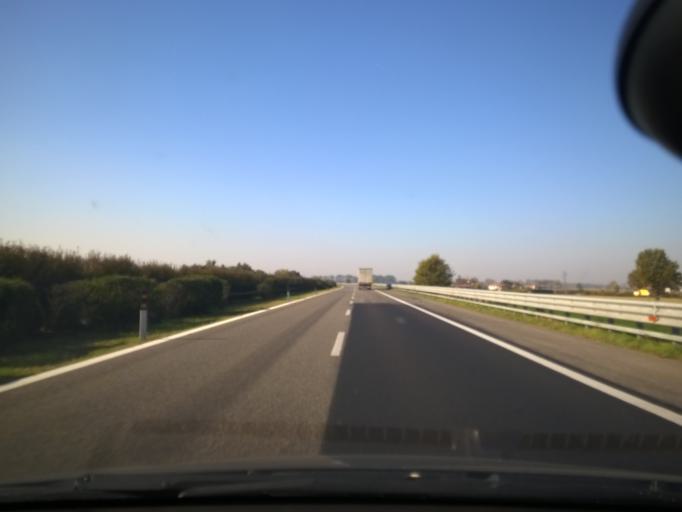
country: IT
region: Emilia-Romagna
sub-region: Provincia di Piacenza
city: Pontenure
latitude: 45.0484
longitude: 9.7941
